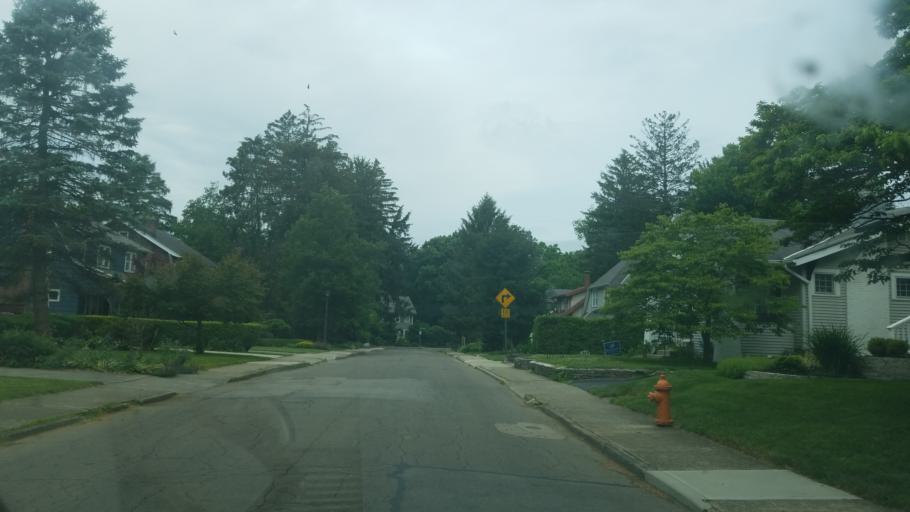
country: US
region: Ohio
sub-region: Franklin County
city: Upper Arlington
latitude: 40.0329
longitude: -83.0229
